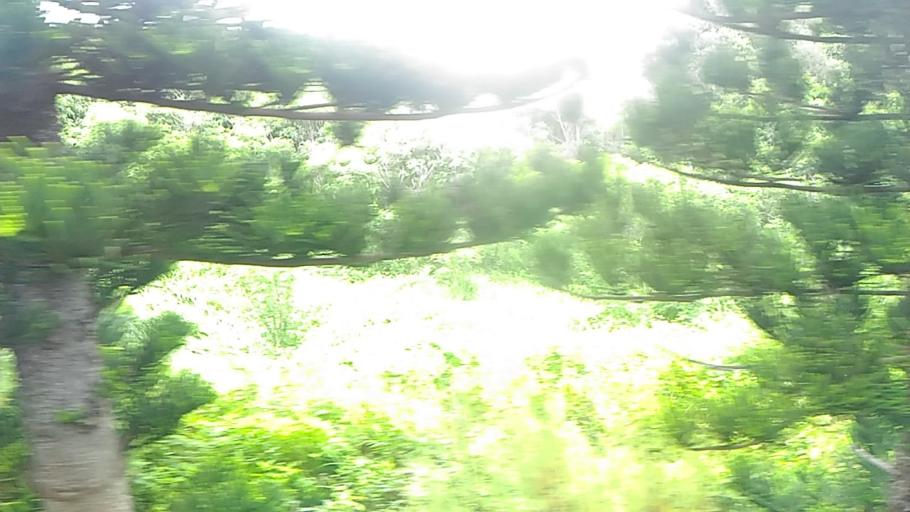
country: TW
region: Taiwan
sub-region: Penghu
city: Ma-kung
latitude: 23.3749
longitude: 119.5053
